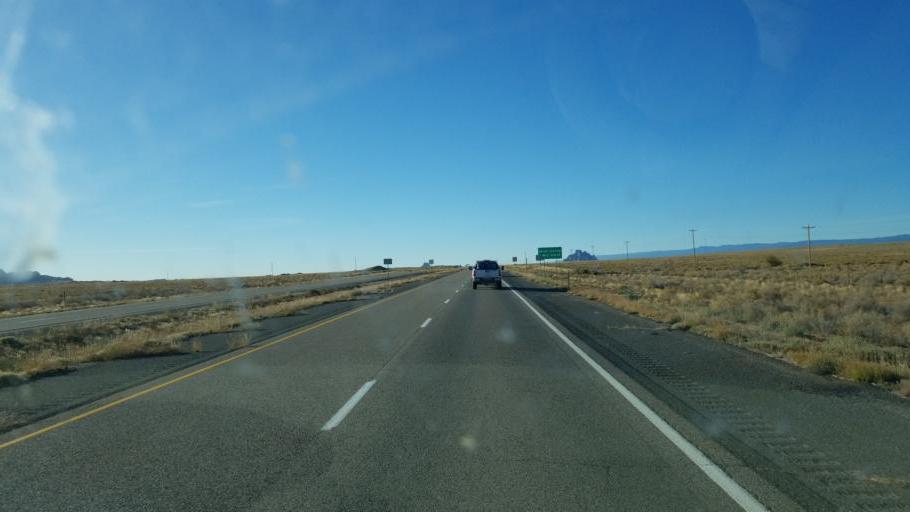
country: US
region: New Mexico
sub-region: San Juan County
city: Shiprock
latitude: 36.4991
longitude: -108.7262
